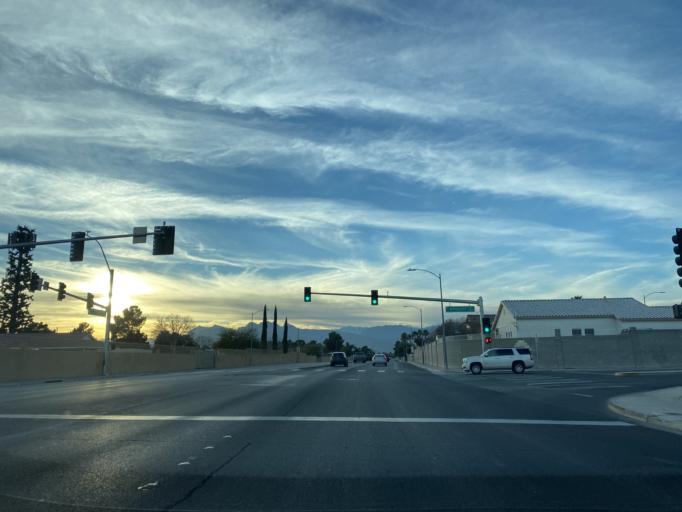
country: US
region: Nevada
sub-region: Clark County
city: North Las Vegas
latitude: 36.2612
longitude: -115.2161
